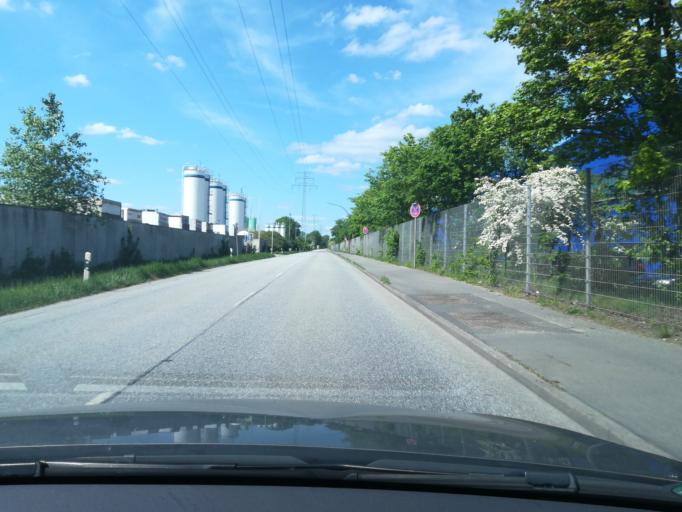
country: DE
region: Hamburg
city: Harburg
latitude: 53.4844
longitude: 9.9794
